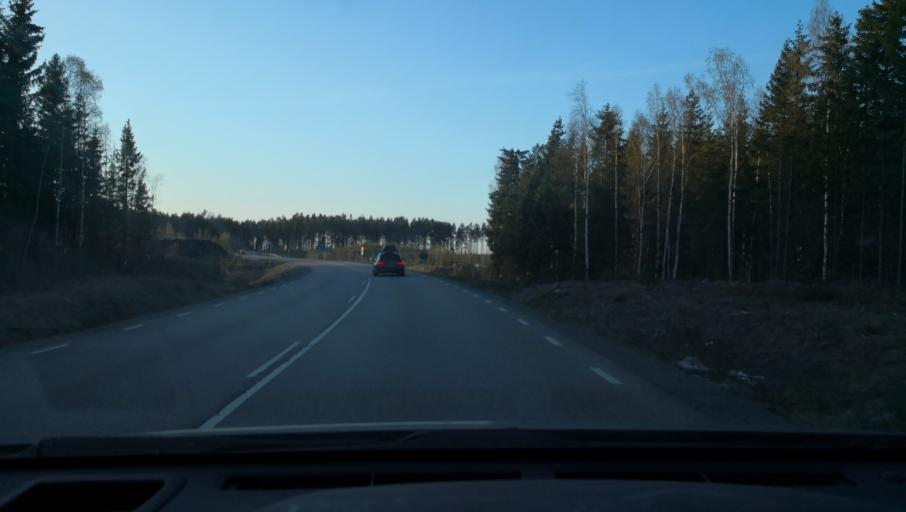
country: SE
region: Uppsala
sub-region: Enkopings Kommun
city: Hummelsta
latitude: 59.6260
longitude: 16.8380
